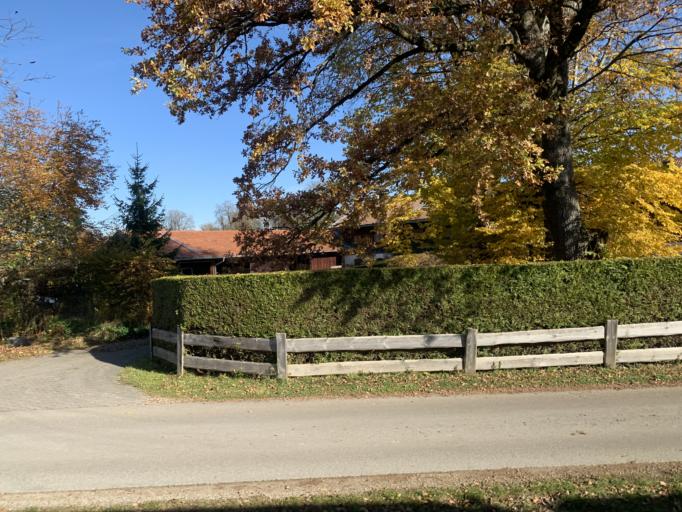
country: DE
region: Bavaria
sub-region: Upper Bavaria
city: Gmund am Tegernsee
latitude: 47.7758
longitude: 11.7113
